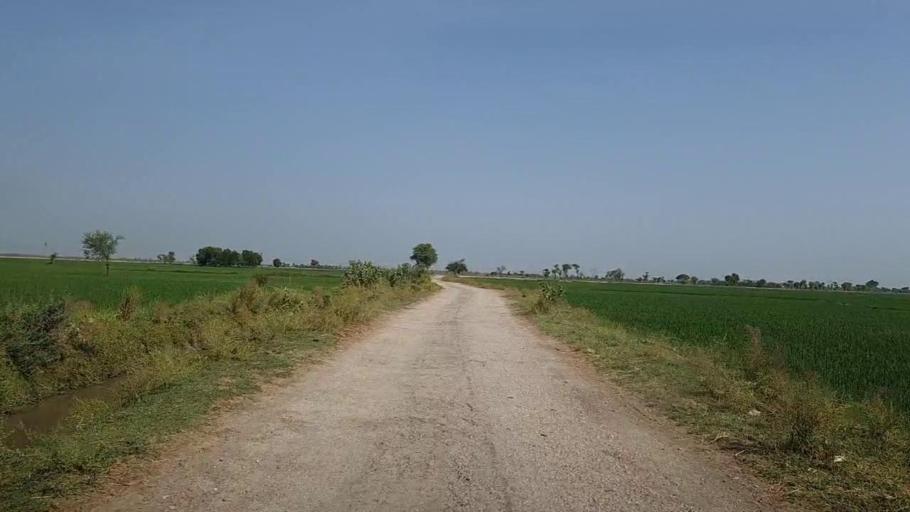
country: PK
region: Sindh
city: Sita Road
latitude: 27.1062
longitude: 67.8506
